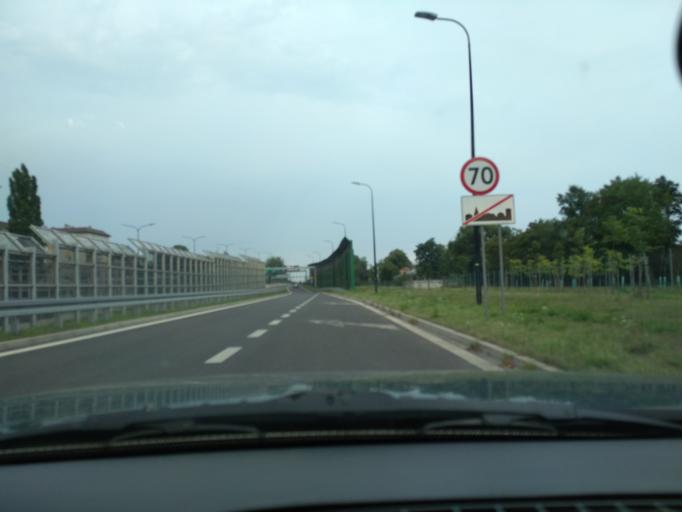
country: PL
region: Silesian Voivodeship
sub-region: Gliwice
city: Gliwice
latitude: 50.2944
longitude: 18.6825
